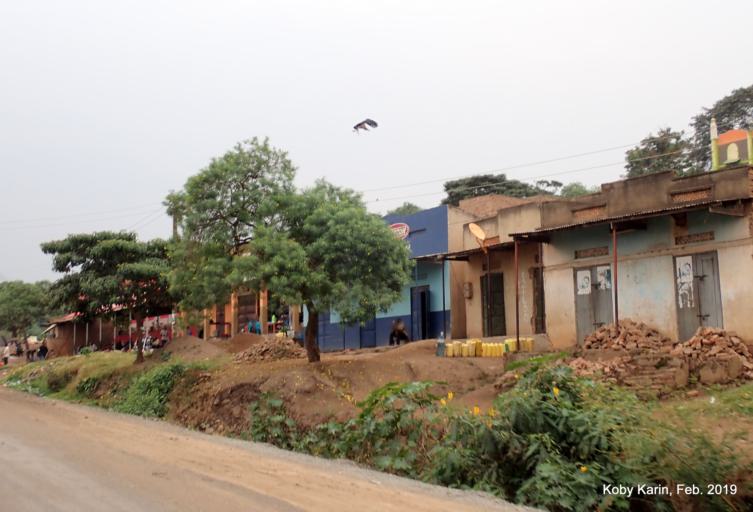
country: UG
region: Western Region
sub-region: Rubirizi District
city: Rubirizi
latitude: -0.2130
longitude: 30.1009
